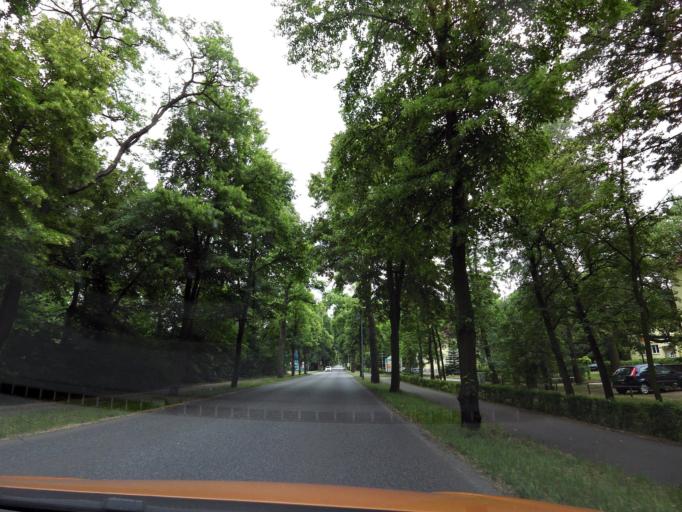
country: DE
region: Brandenburg
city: Zossen
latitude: 52.1721
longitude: 13.4703
